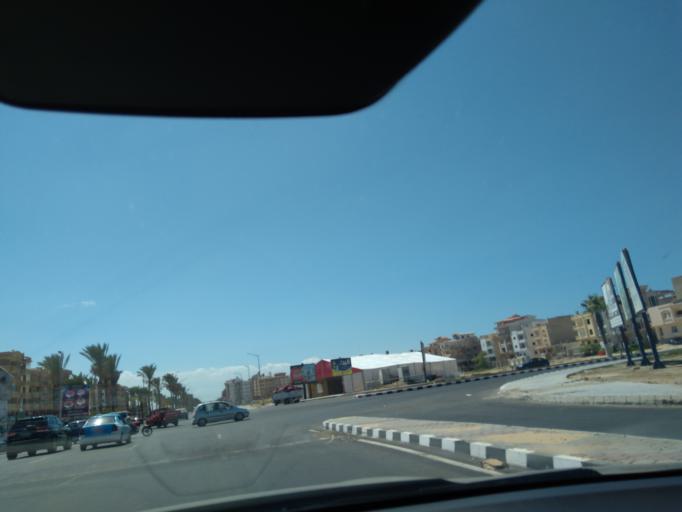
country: EG
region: Dumyat
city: Faraskur
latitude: 31.4397
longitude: 31.6742
